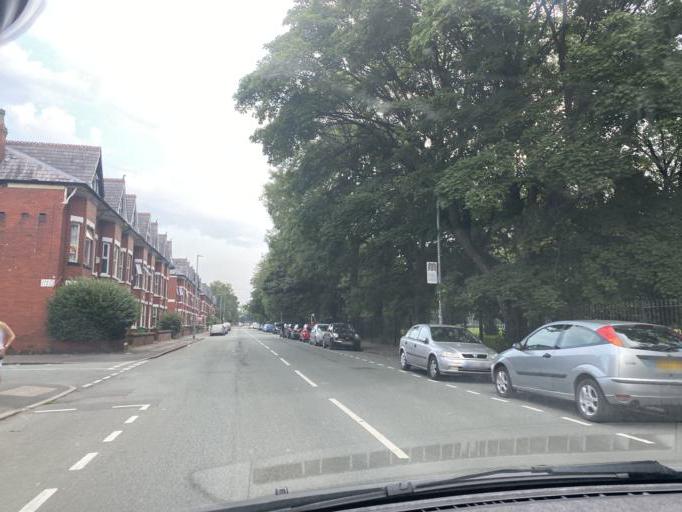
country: GB
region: England
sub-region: Manchester
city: Fallowfield
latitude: 53.4498
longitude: -2.2286
